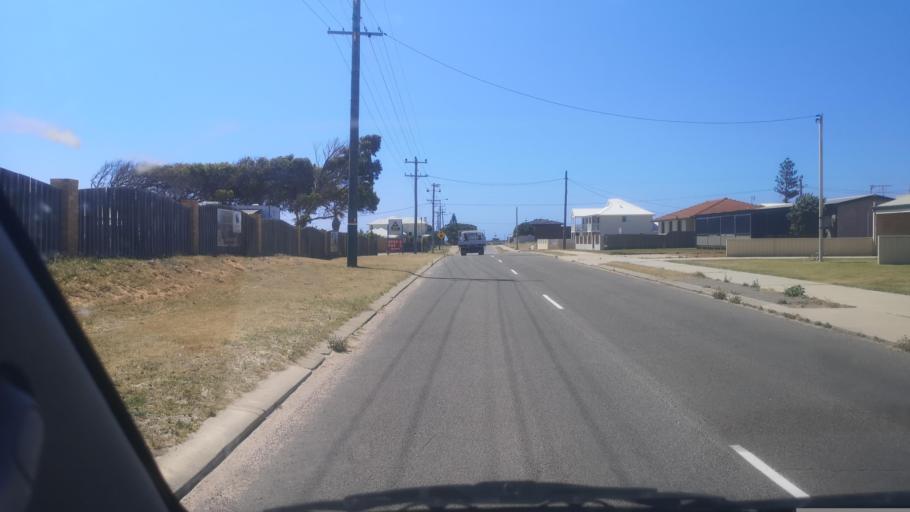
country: AU
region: Western Australia
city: Port Denison
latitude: -29.2783
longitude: 114.9187
